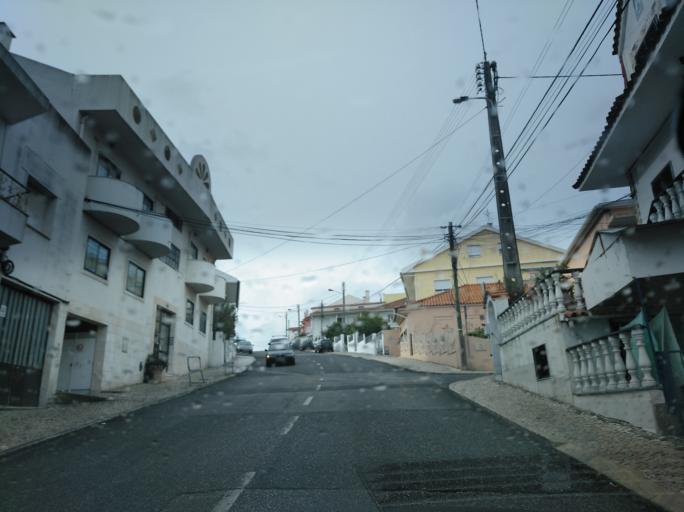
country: PT
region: Lisbon
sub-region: Odivelas
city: Famoes
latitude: 38.7934
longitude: -9.2179
